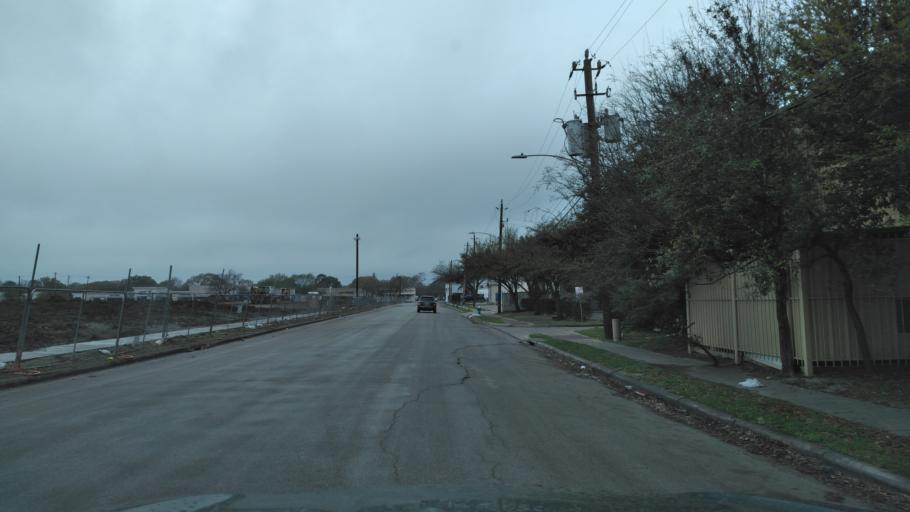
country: US
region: Texas
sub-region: Harris County
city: Piney Point Village
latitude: 29.7306
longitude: -95.4984
